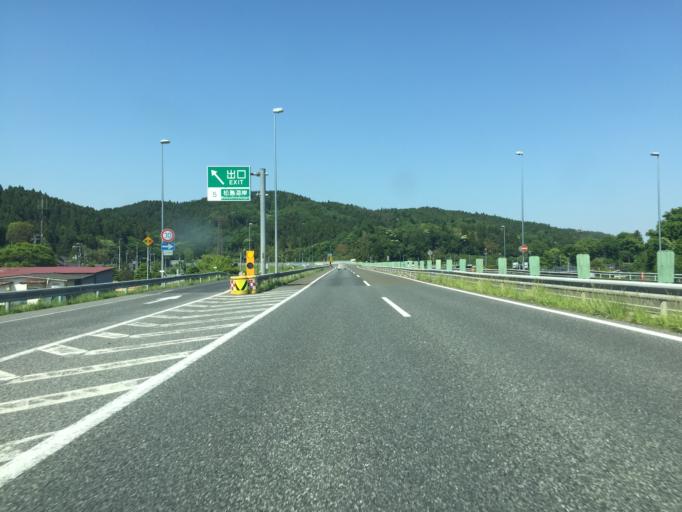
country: JP
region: Miyagi
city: Matsushima
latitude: 38.3626
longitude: 141.0292
